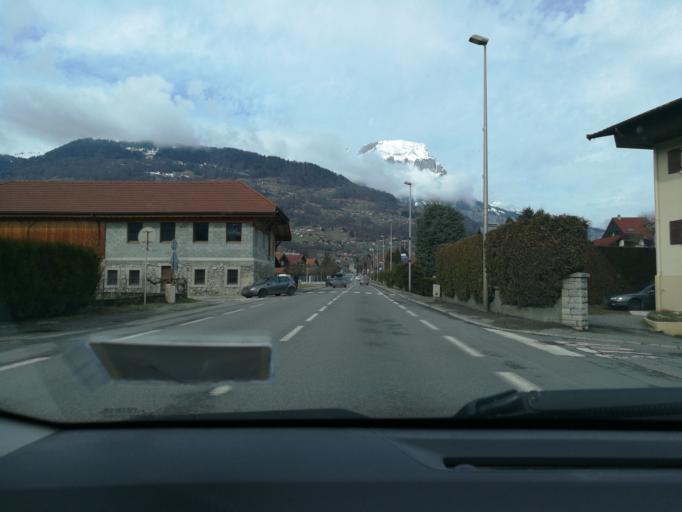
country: FR
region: Rhone-Alpes
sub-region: Departement de la Haute-Savoie
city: Sallanches
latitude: 45.9288
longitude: 6.6379
